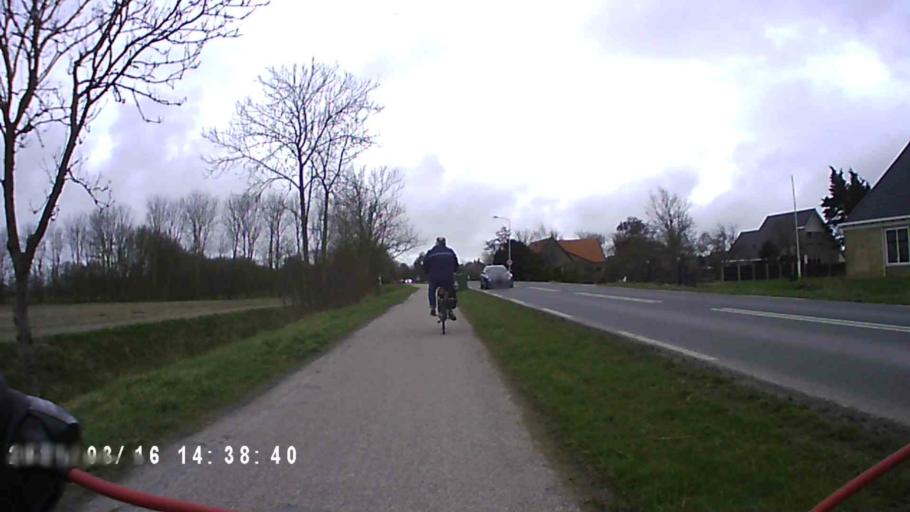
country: NL
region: Friesland
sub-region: Gemeente Harlingen
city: Harlingen
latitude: 53.1428
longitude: 5.4318
